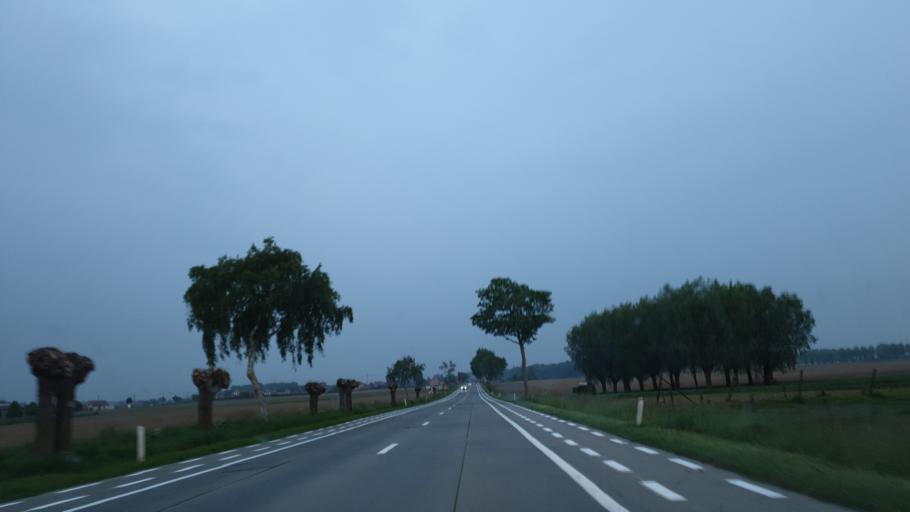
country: BE
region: Flanders
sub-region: Provincie West-Vlaanderen
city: Poperinge
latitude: 50.8944
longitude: 2.8002
